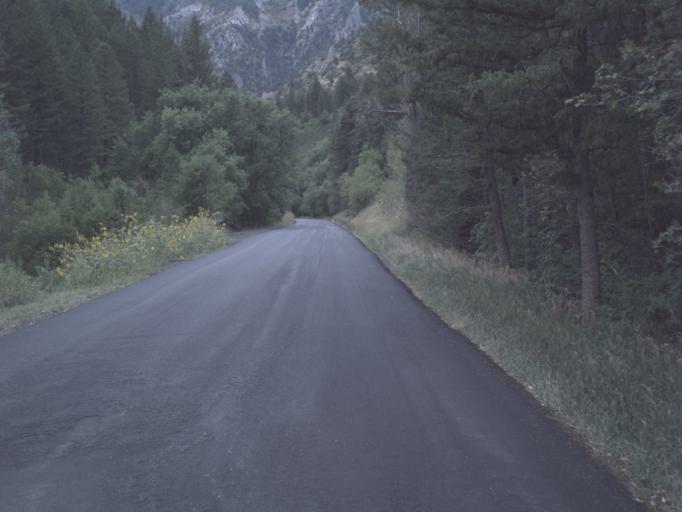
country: US
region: Utah
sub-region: Utah County
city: Cedar Hills
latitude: 40.4484
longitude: -111.6448
